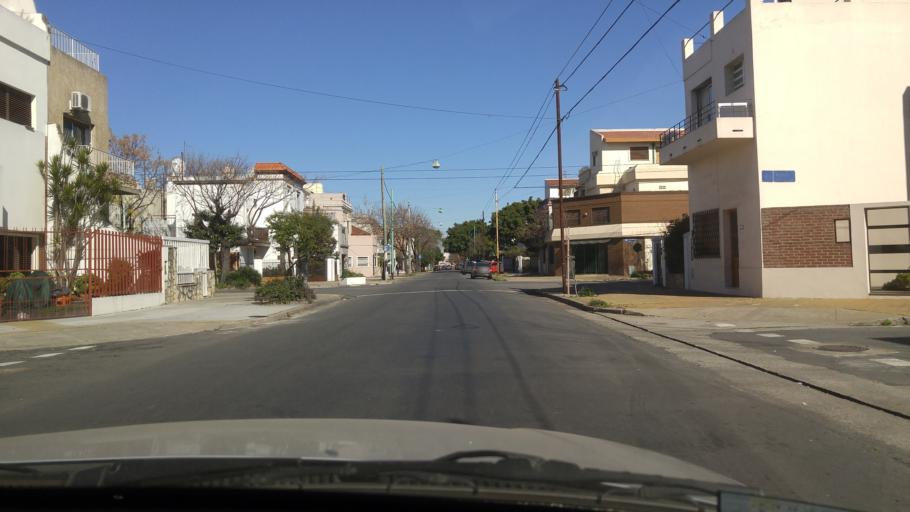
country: AR
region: Buenos Aires F.D.
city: Villa Santa Rita
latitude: -34.6221
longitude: -58.4928
